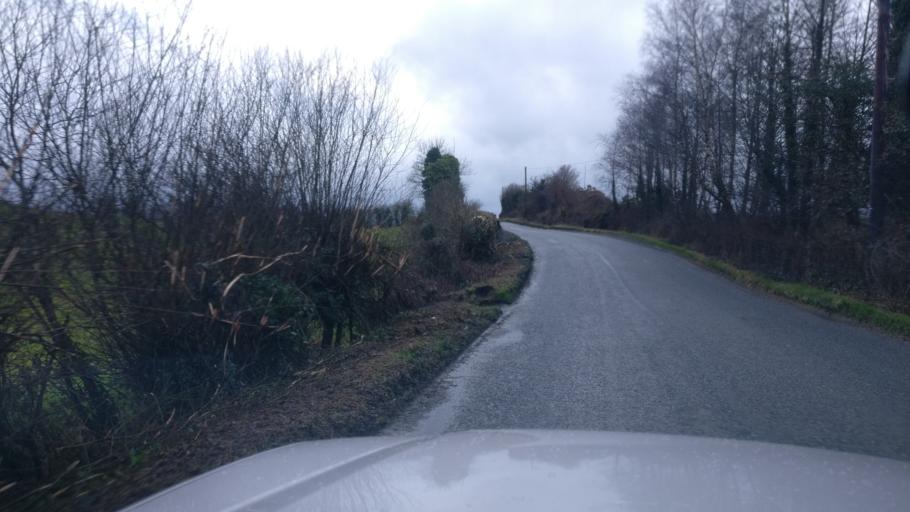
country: IE
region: Leinster
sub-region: An Iarmhi
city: Athlone
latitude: 53.4191
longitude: -8.0588
